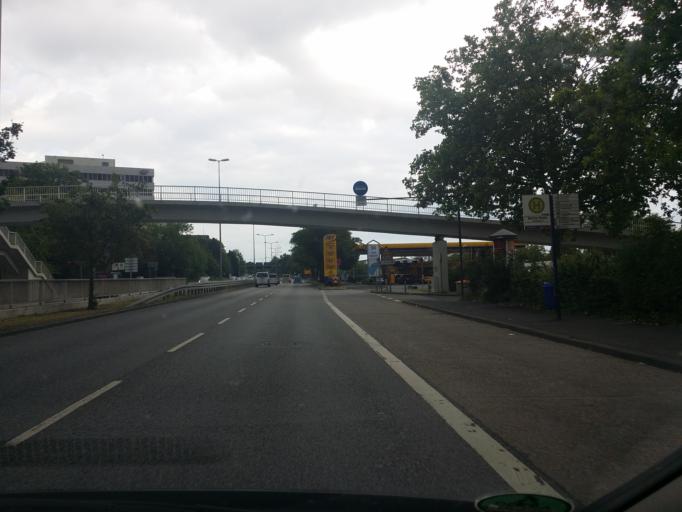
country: DE
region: Hesse
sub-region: Regierungsbezirk Darmstadt
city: Wiesbaden
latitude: 50.0712
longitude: 8.2586
